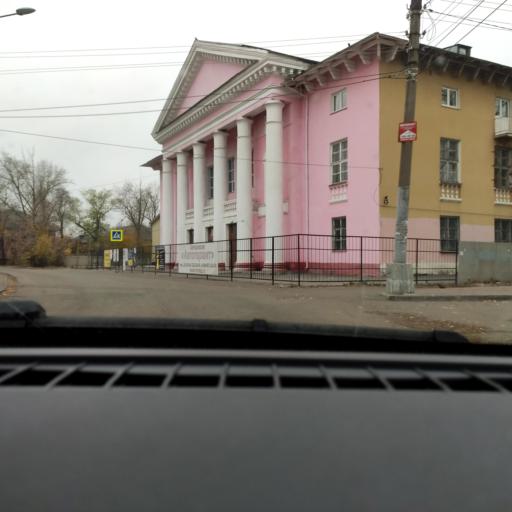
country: RU
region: Voronezj
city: Voronezh
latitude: 51.6649
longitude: 39.2775
